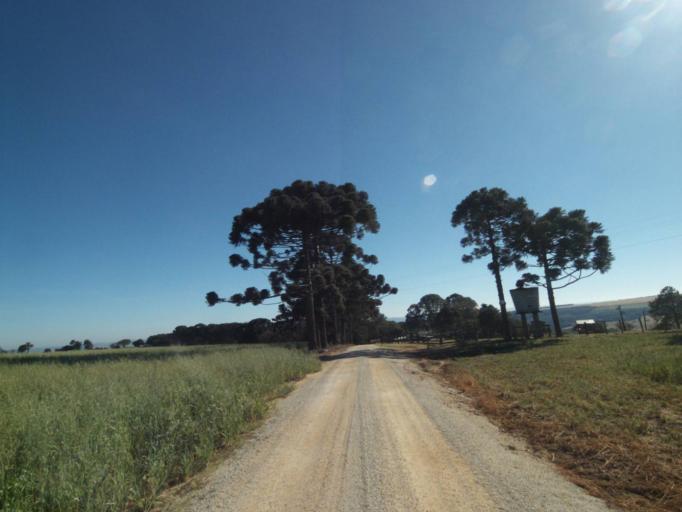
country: BR
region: Parana
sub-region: Tibagi
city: Tibagi
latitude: -24.5265
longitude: -50.3104
